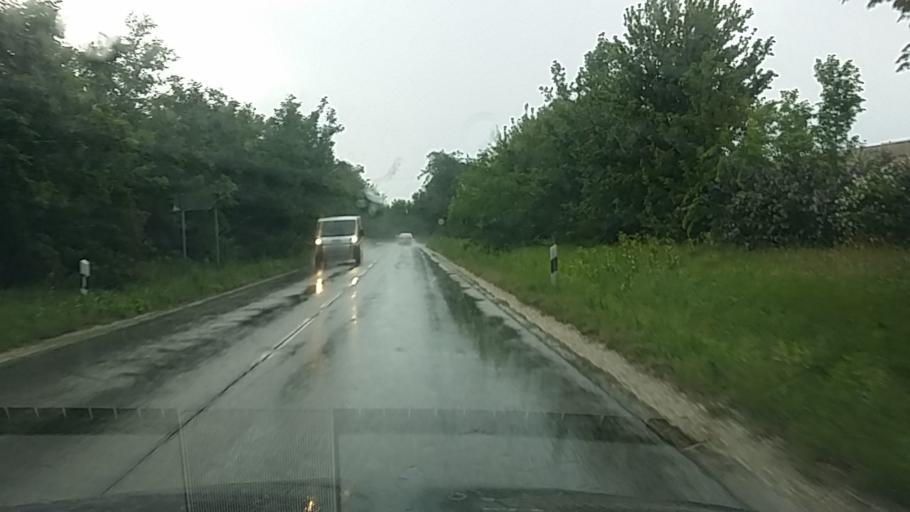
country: HU
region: Pest
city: Inarcs
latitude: 47.3128
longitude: 19.2917
